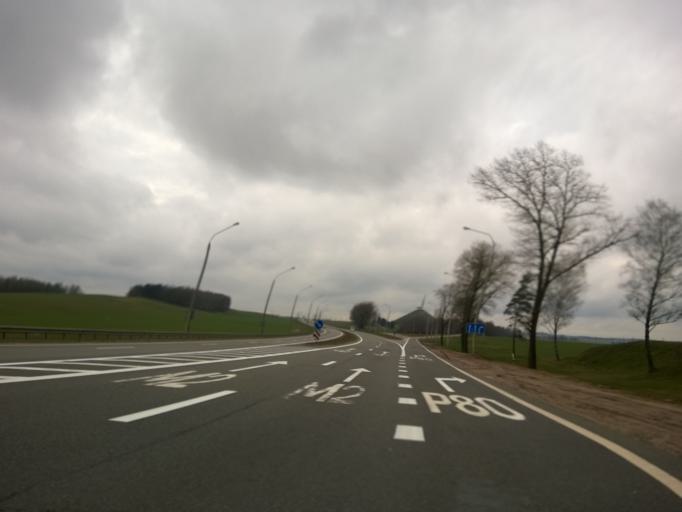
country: BY
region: Minsk
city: Slabada
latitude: 54.0215
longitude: 27.9177
